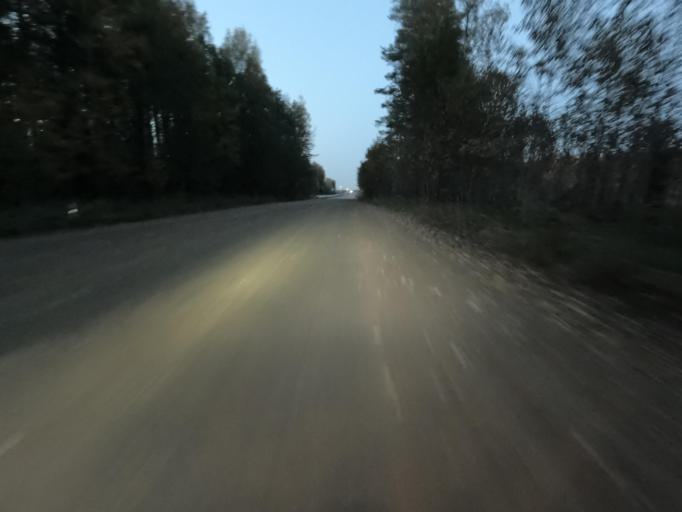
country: RU
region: Leningrad
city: Lyuban'
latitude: 59.1923
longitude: 31.2519
